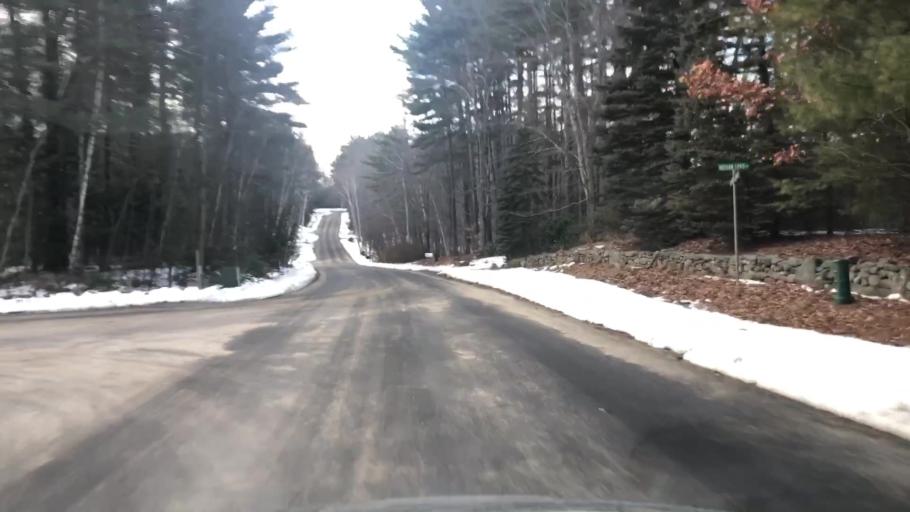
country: US
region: New Hampshire
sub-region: Hillsborough County
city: Milford
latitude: 42.8549
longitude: -71.6258
